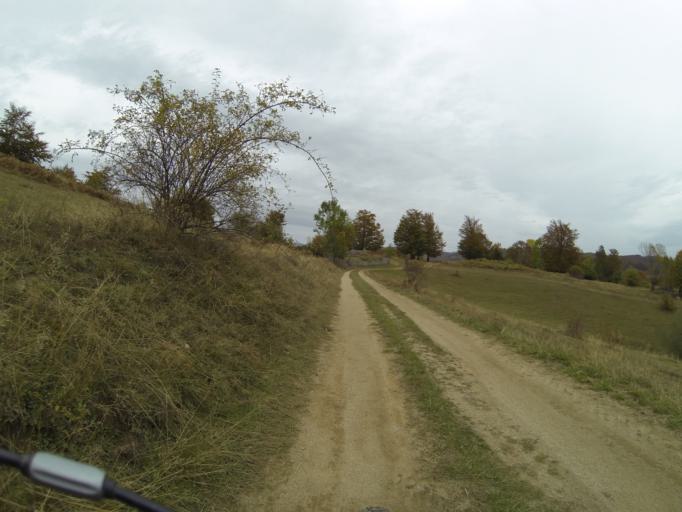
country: RO
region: Gorj
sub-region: Comuna Pades
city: Closani
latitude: 45.1183
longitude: 22.8506
